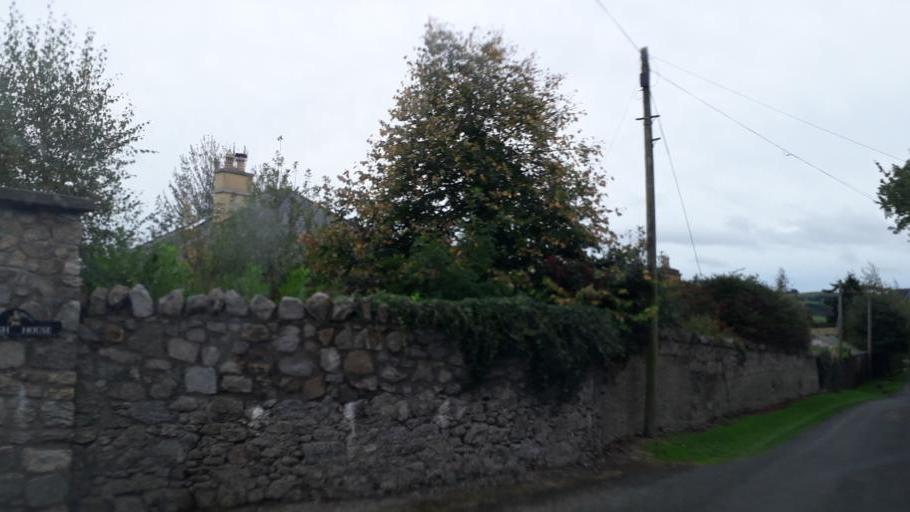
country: IE
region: Leinster
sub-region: Wicklow
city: Enniskerry
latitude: 53.1775
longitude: -6.2039
